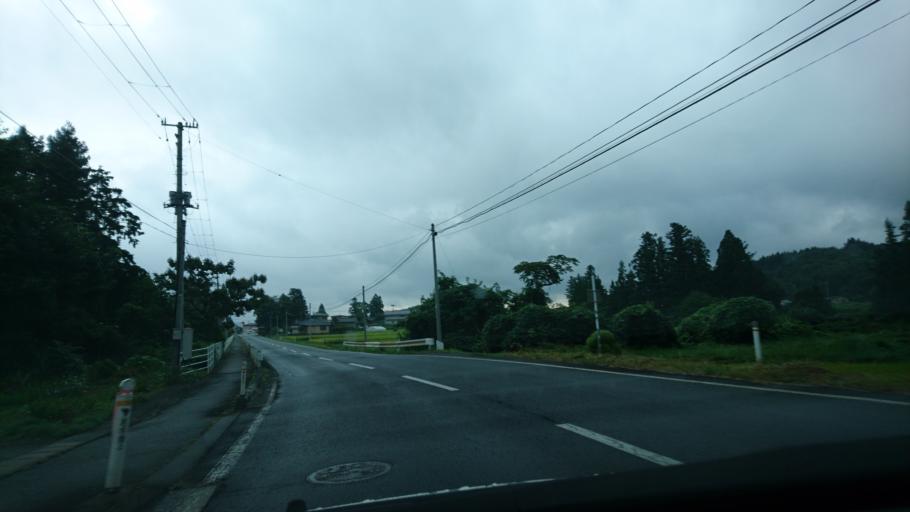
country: JP
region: Iwate
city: Ichinoseki
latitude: 38.9176
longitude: 141.0879
